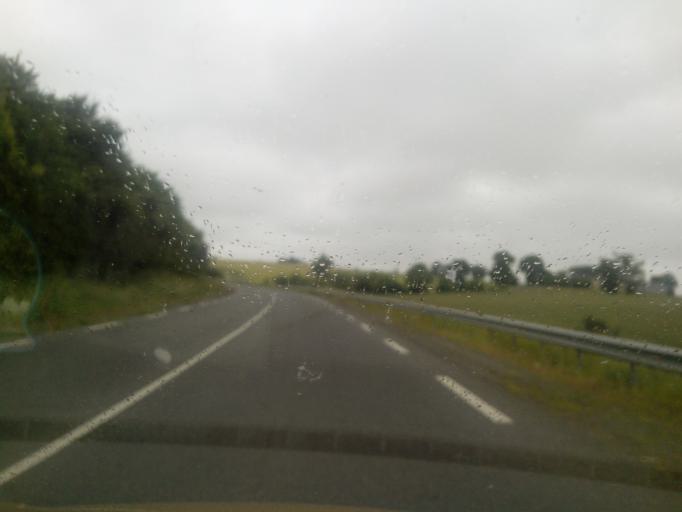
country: FR
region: Brittany
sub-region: Departement d'Ille-et-Vilaine
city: Chasne-sur-Illet
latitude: 48.2601
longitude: -1.5992
